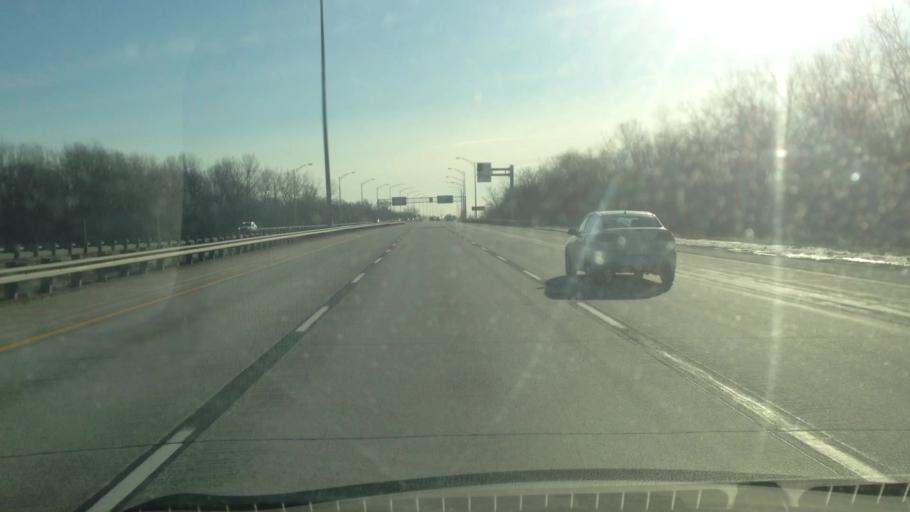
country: CA
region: Quebec
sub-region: Laurentides
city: Boisbriand
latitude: 45.5859
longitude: -73.8434
